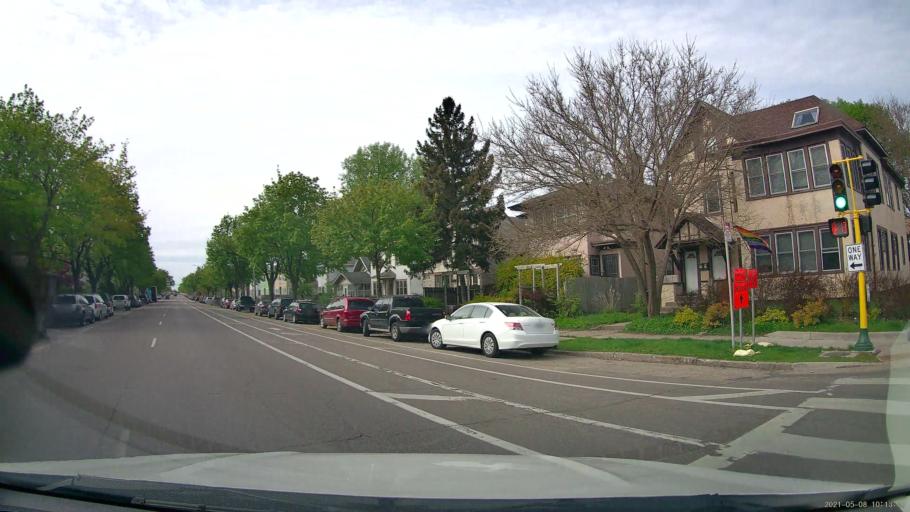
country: US
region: Minnesota
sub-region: Hennepin County
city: Minneapolis
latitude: 44.9395
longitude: -93.2676
